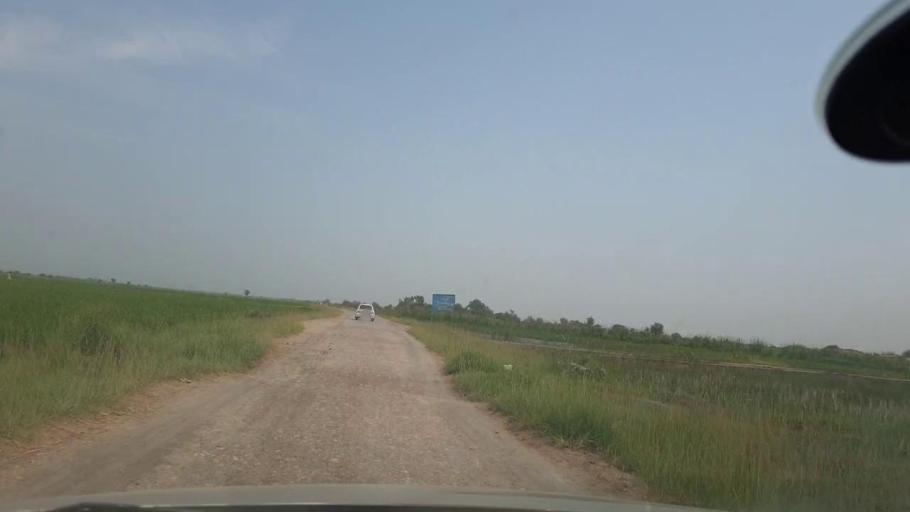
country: PK
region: Sindh
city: Jacobabad
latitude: 28.1420
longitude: 68.3568
